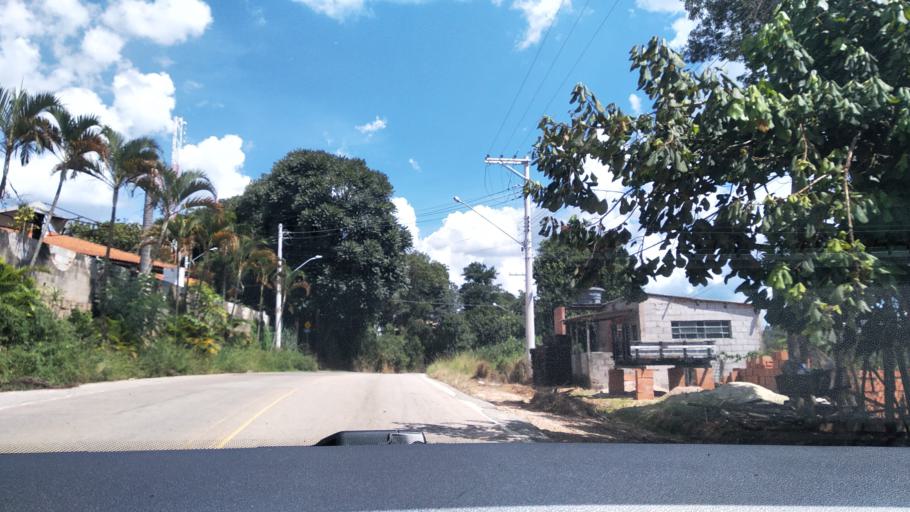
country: BR
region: Sao Paulo
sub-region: Varzea Paulista
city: Varzea Paulista
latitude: -23.2455
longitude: -46.8750
